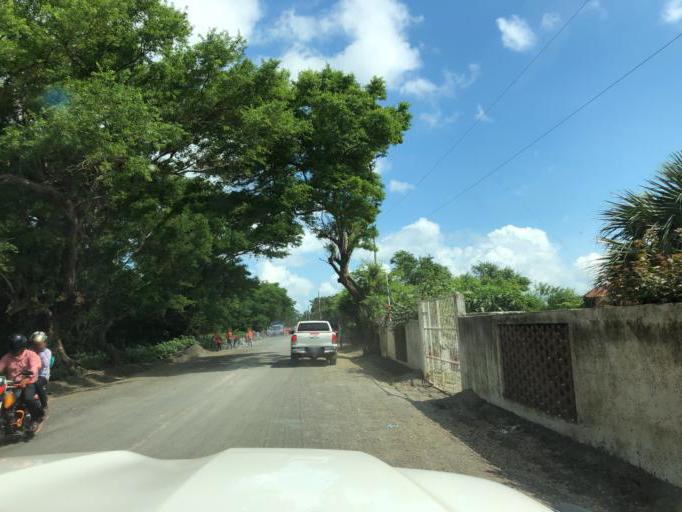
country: NI
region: Granada
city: Granada
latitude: 12.0092
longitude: -85.9324
